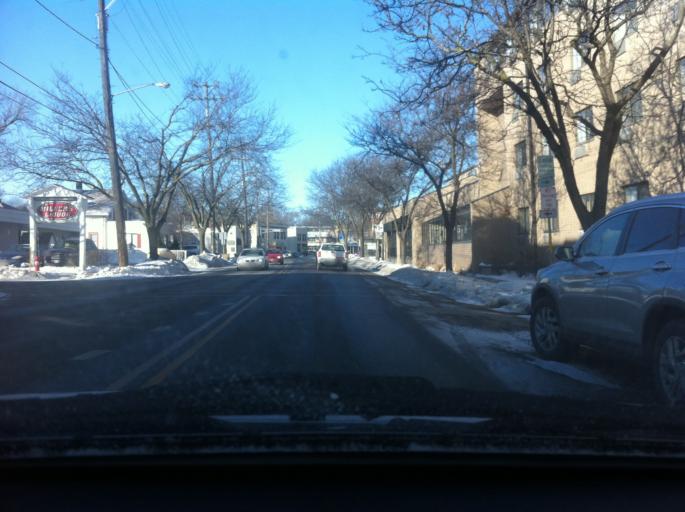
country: US
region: Wisconsin
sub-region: Dane County
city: Shorewood Hills
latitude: 43.0721
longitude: -89.4259
